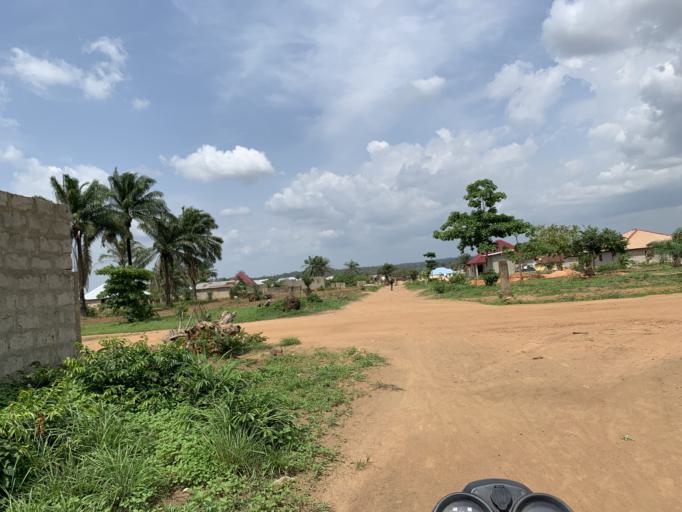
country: SL
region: Western Area
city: Waterloo
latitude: 8.3596
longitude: -13.0447
